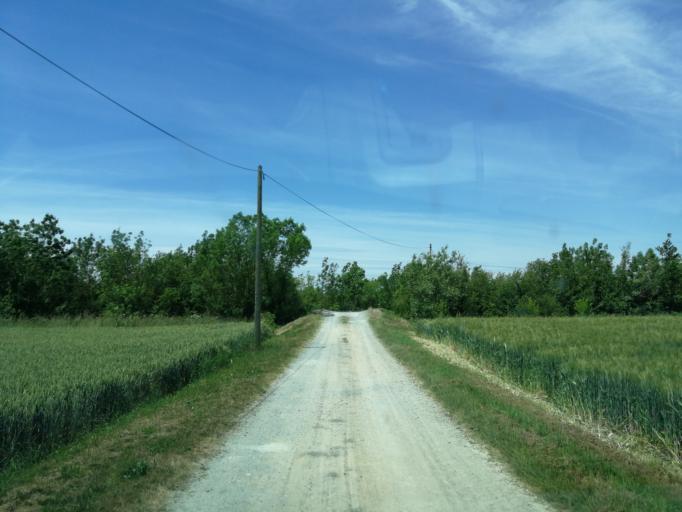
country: FR
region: Pays de la Loire
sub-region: Departement de la Vendee
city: Le Langon
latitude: 46.3772
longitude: -0.9499
